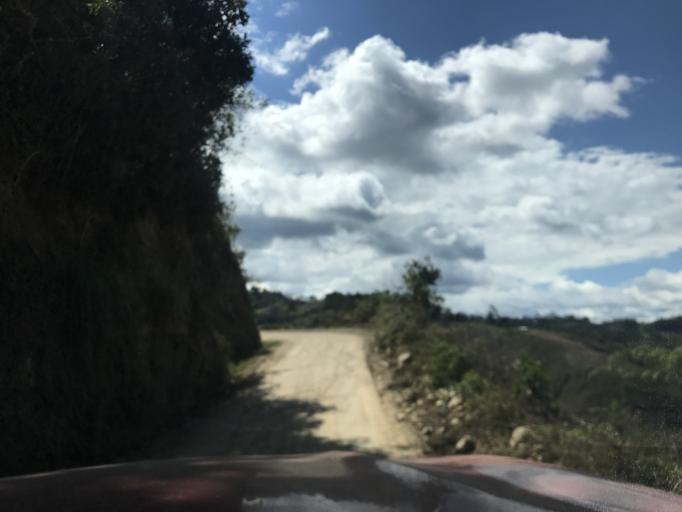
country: PE
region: Cajamarca
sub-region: Provincia de Chota
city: Querocoto
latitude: -6.3503
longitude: -79.0389
